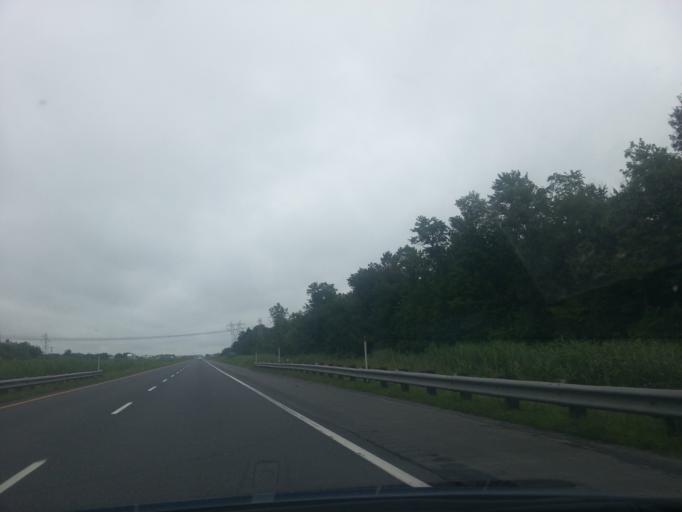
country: CA
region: Quebec
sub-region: Centre-du-Quebec
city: Drummondville
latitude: 45.9191
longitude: -72.4765
